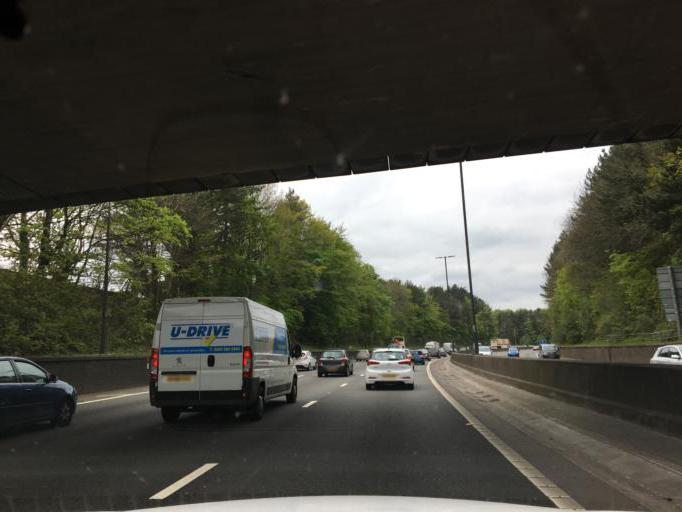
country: GB
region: Wales
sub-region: Newport
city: Newport
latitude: 51.5802
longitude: -3.0348
